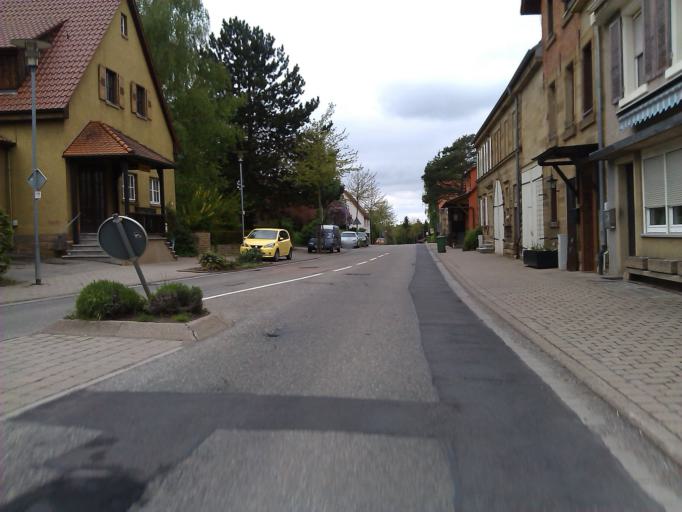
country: DE
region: Baden-Wuerttemberg
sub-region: Karlsruhe Region
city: Sternenfels
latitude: 49.0515
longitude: 8.8488
